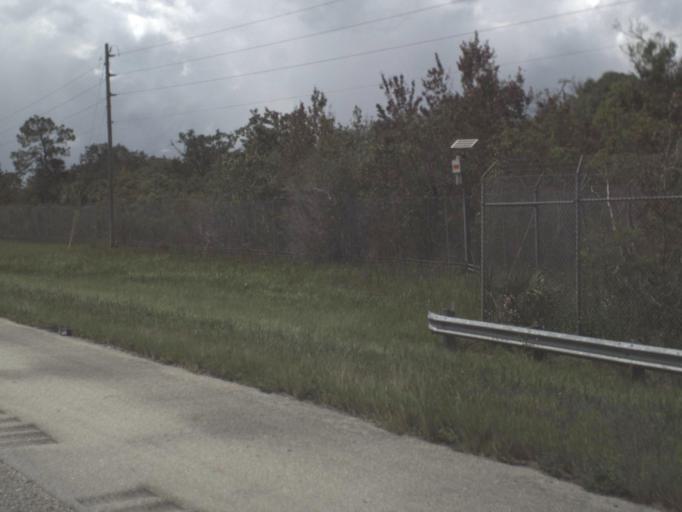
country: US
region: Florida
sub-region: Collier County
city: Immokalee
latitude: 26.1586
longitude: -81.2534
